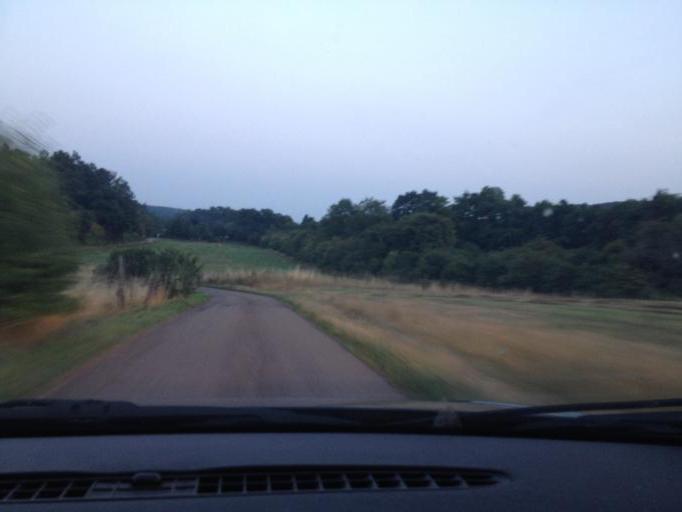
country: DE
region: Saarland
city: Namborn
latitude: 49.5493
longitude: 7.1337
